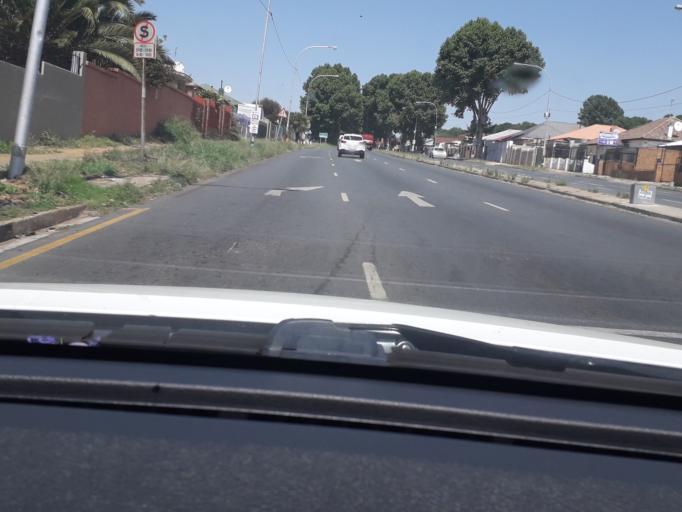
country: ZA
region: Gauteng
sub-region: City of Johannesburg Metropolitan Municipality
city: Johannesburg
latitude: -26.1867
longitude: 28.0980
